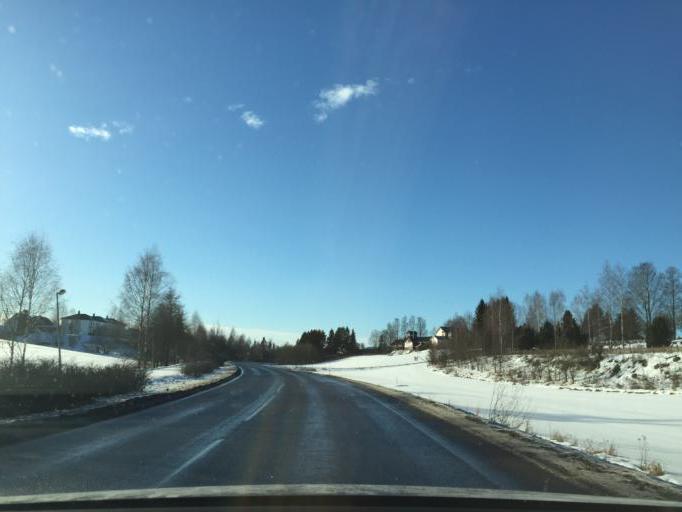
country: NO
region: Akershus
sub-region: Nes
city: Arnes
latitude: 60.1253
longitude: 11.4765
